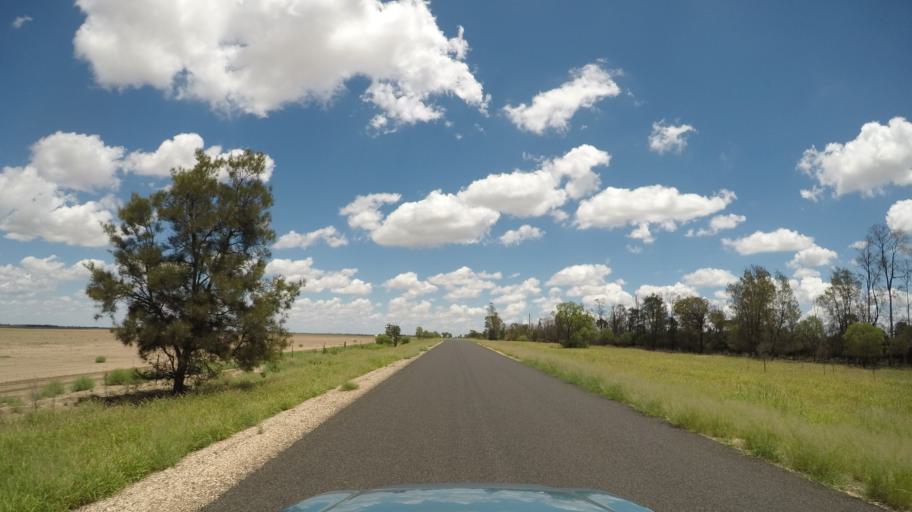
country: AU
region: Queensland
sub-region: Goondiwindi
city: Goondiwindi
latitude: -28.1630
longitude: 150.1523
